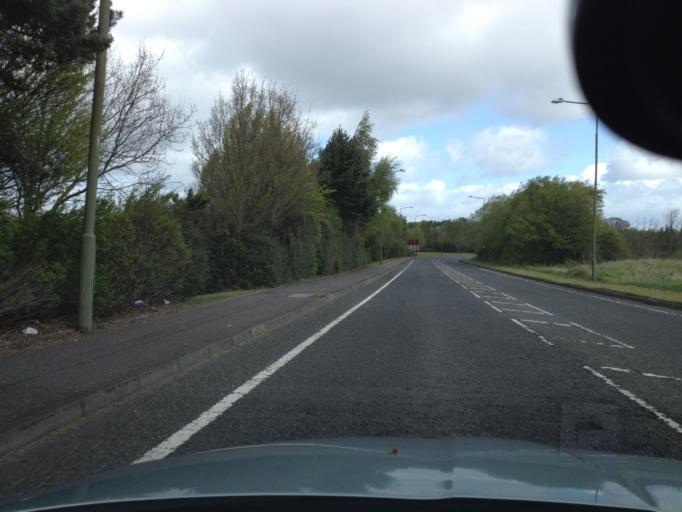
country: GB
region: Scotland
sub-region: West Lothian
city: Livingston
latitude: 55.8747
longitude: -3.5418
